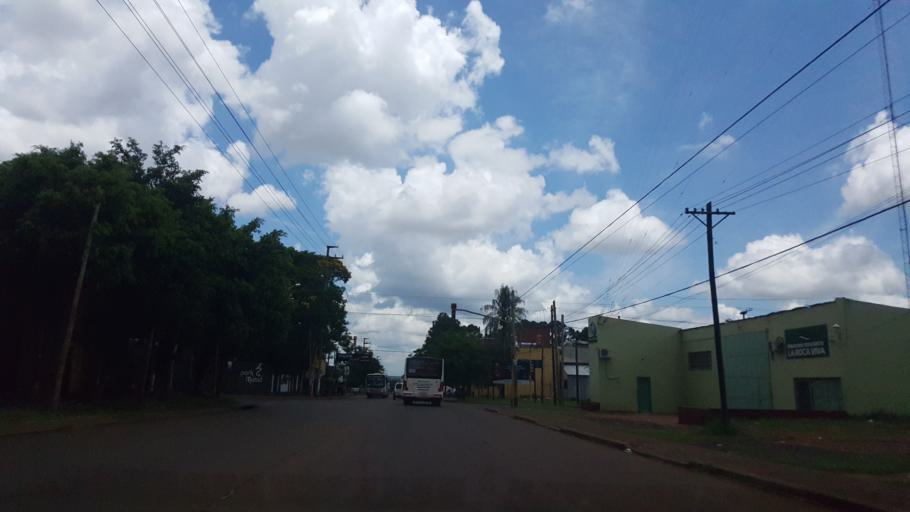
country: AR
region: Misiones
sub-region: Departamento de Capital
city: Posadas
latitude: -27.3960
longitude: -55.9130
